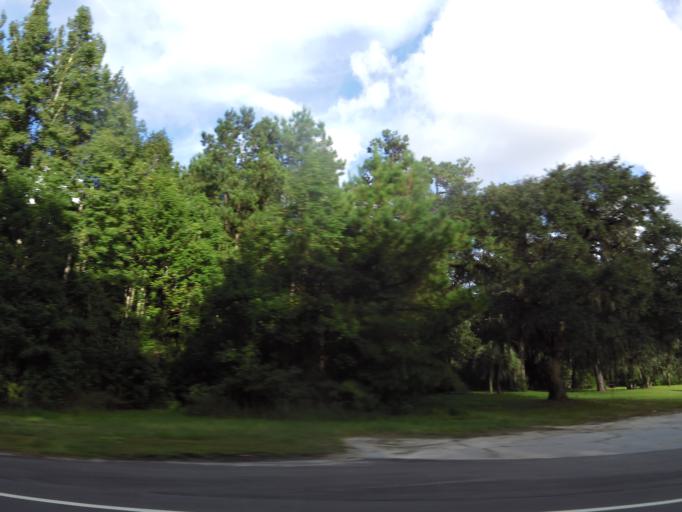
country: US
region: Georgia
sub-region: Liberty County
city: Midway
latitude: 31.8121
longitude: -81.4304
